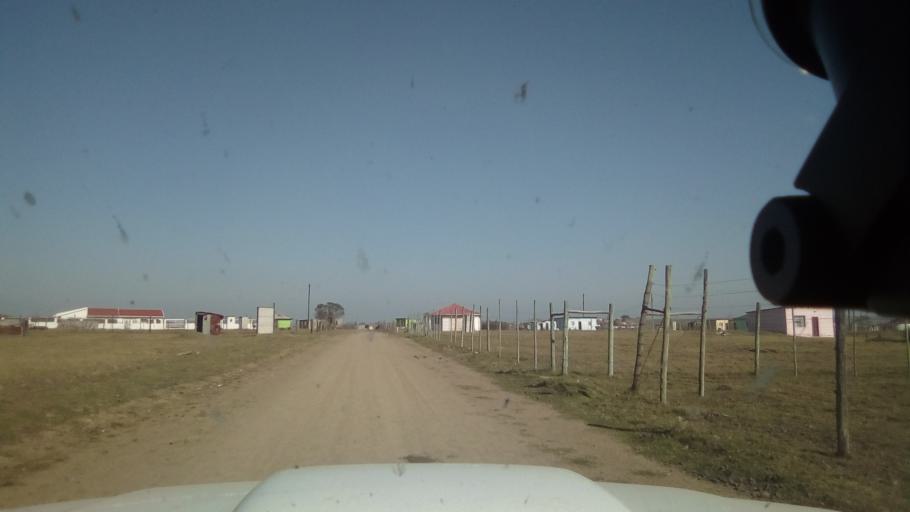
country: ZA
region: Eastern Cape
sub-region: Buffalo City Metropolitan Municipality
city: Bhisho
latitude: -32.9417
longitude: 27.3352
